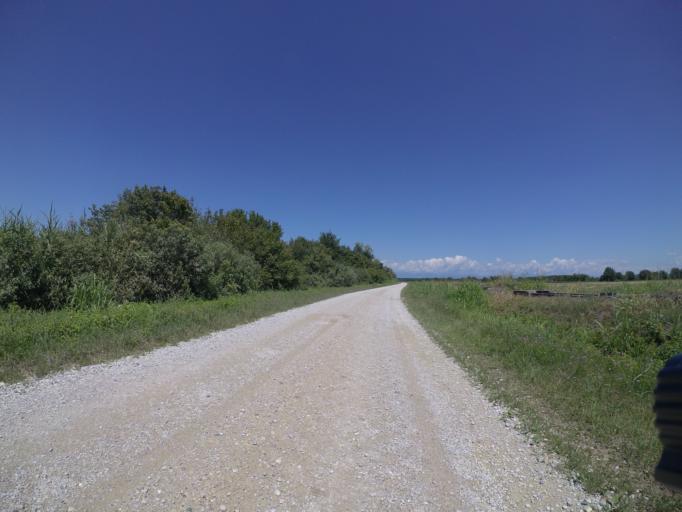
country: IT
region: Friuli Venezia Giulia
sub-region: Provincia di Udine
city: Teor
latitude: 45.8845
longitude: 13.0897
